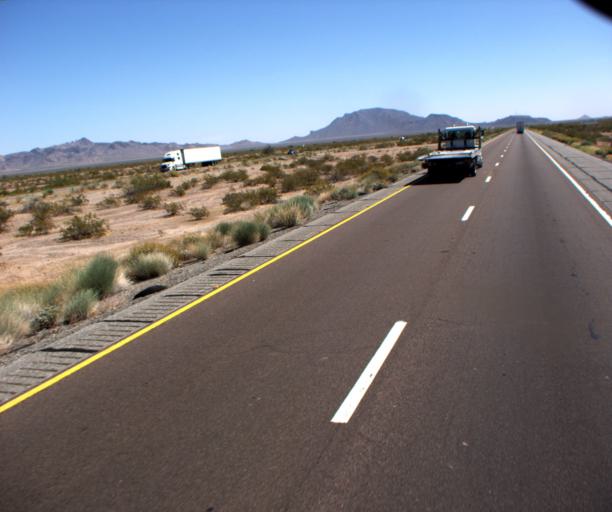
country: US
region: Arizona
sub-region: La Paz County
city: Salome
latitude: 33.5448
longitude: -113.1956
